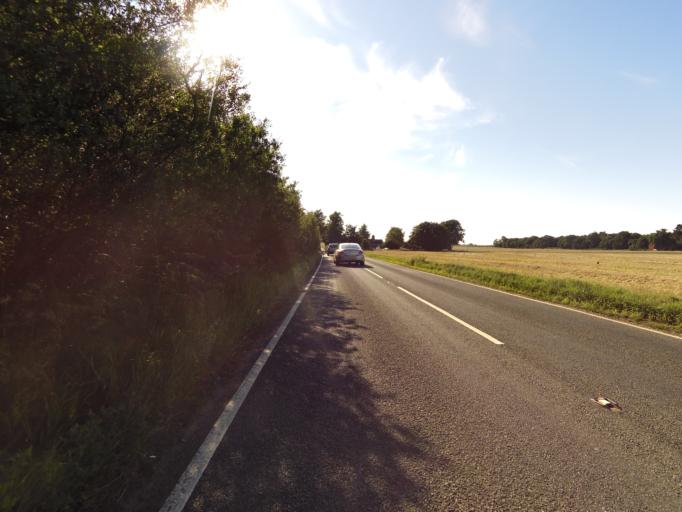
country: GB
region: England
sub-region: Suffolk
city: Kesgrave
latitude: 52.0506
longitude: 1.2573
